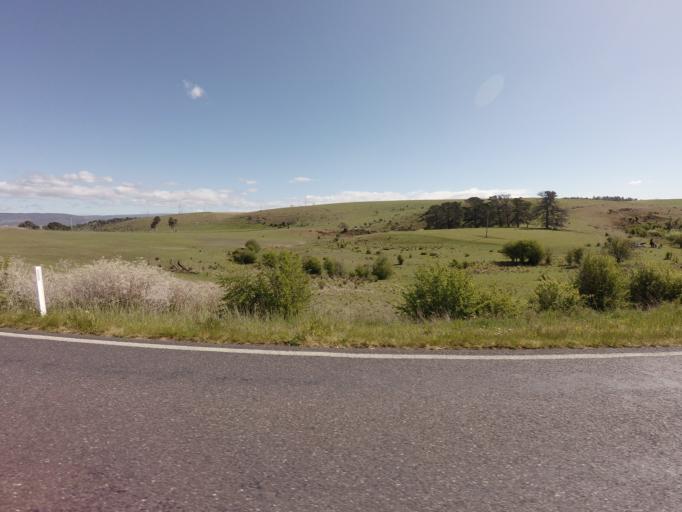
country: AU
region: Tasmania
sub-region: Derwent Valley
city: New Norfolk
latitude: -42.6533
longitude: 146.9358
